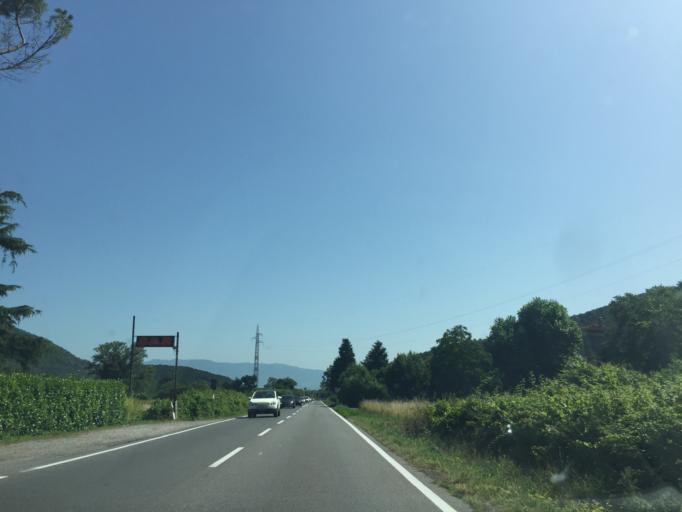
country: IT
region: Tuscany
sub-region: Province of Pisa
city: Asciano
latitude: 43.7838
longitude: 10.4663
